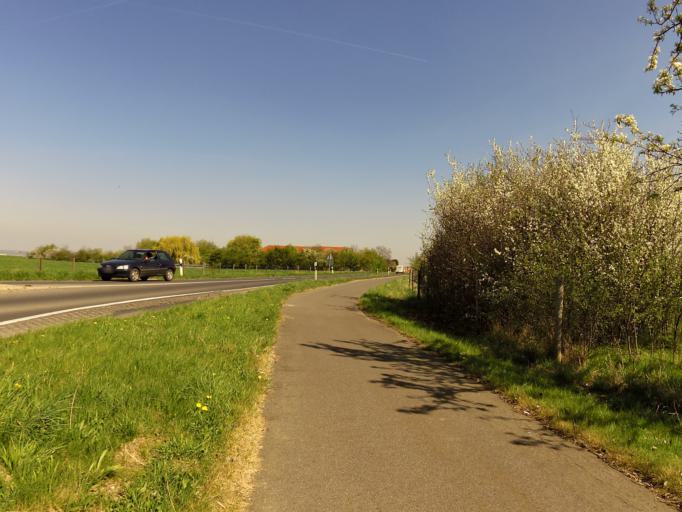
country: DE
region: North Rhine-Westphalia
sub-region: Regierungsbezirk Koln
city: Rheinbach
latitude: 50.6282
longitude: 6.8882
